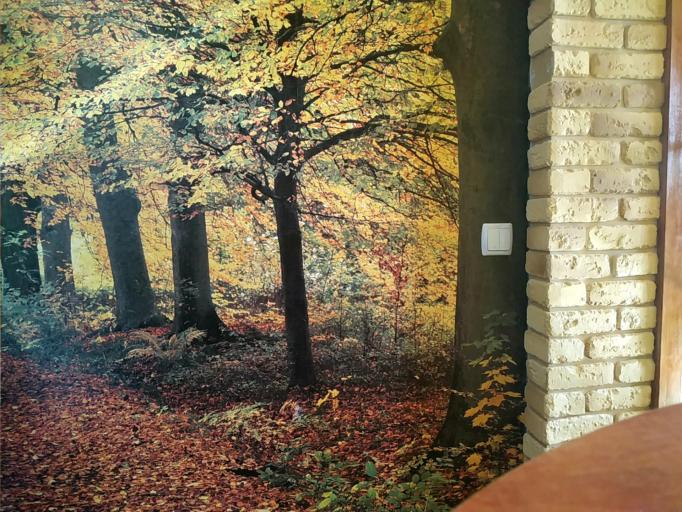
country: RU
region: Jaroslavl
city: Kukoboy
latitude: 58.8165
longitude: 39.7679
